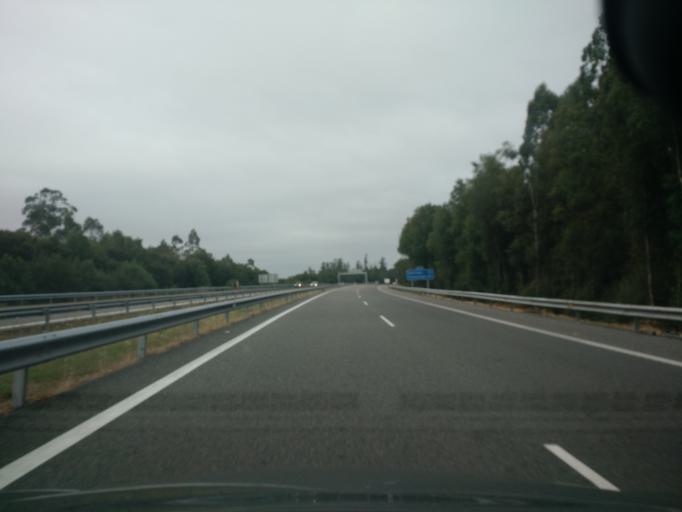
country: ES
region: Galicia
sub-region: Provincia da Coruna
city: Ordes
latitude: 43.0736
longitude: -8.3598
